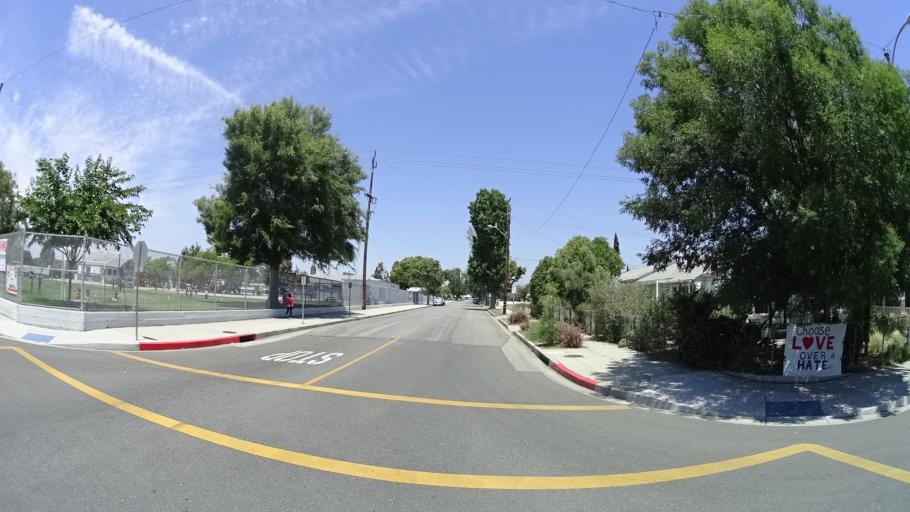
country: US
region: California
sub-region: Los Angeles County
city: Burbank
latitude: 34.1769
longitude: -118.3323
